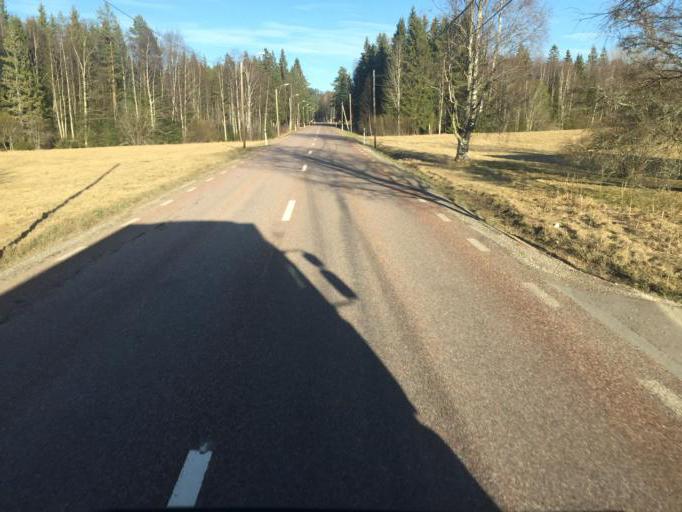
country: SE
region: Dalarna
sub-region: Gagnefs Kommun
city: Mockfjard
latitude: 60.5076
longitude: 14.8324
